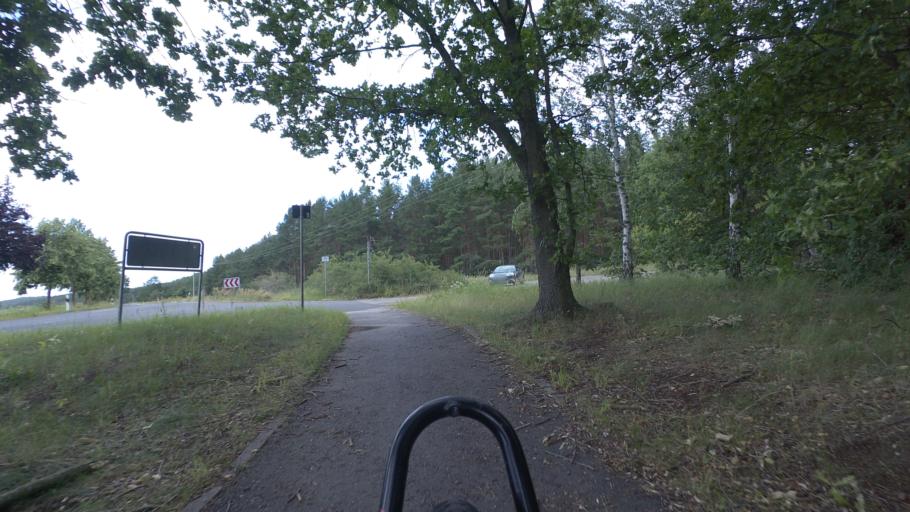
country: DE
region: Brandenburg
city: Trebbin
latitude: 52.2332
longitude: 13.1939
